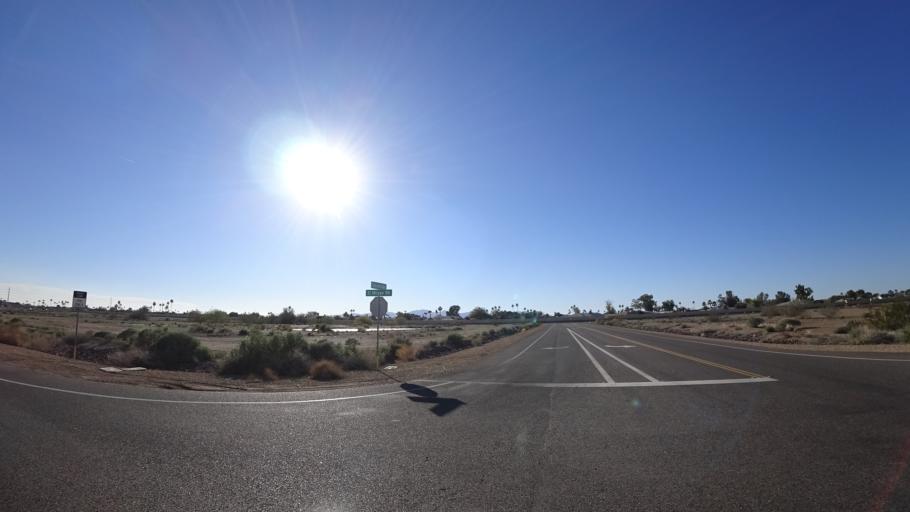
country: US
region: Arizona
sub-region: Maricopa County
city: Surprise
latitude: 33.6461
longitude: -112.3229
